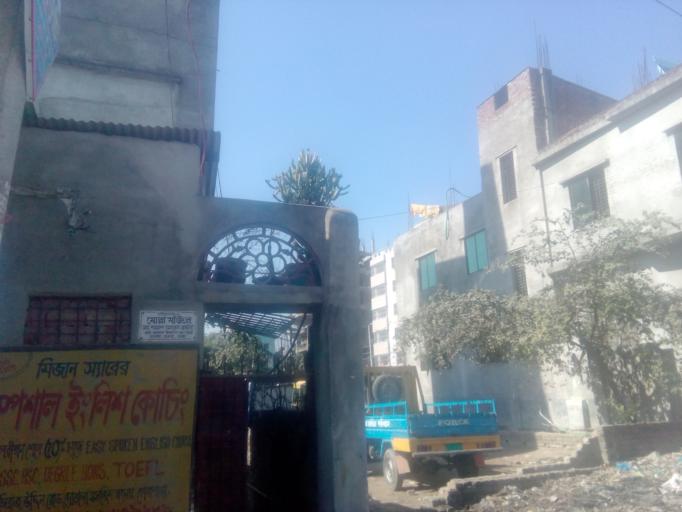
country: BD
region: Dhaka
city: Paltan
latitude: 23.7082
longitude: 90.4747
